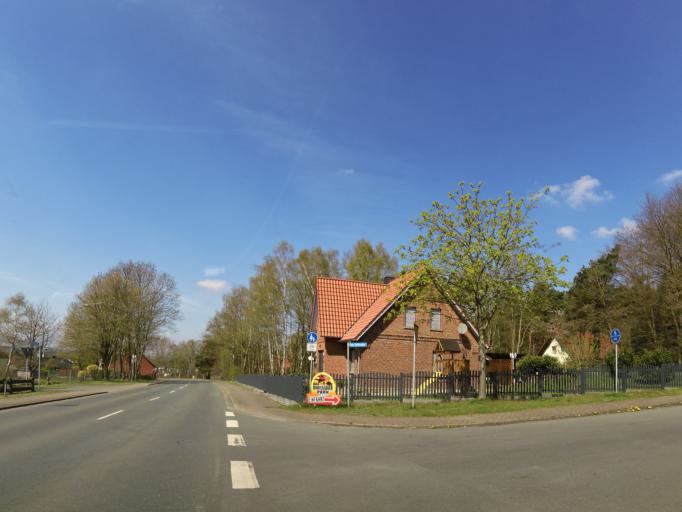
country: DE
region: Lower Saxony
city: Rehburg-Loccum
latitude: 52.4394
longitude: 9.2025
